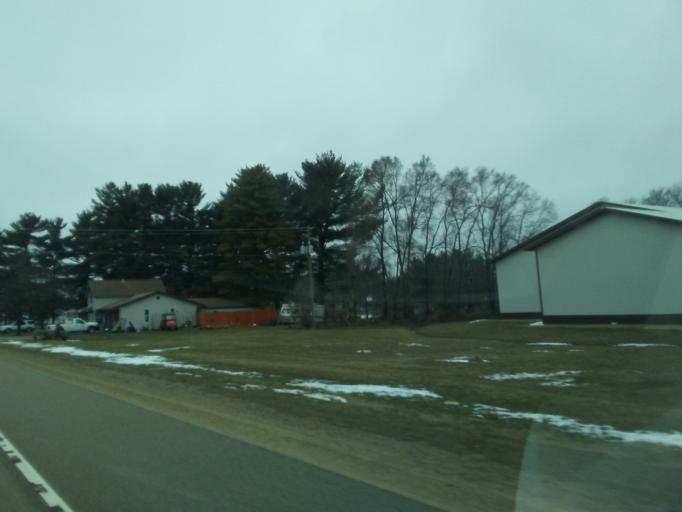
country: US
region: Wisconsin
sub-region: Dane County
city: Mazomanie
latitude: 43.1617
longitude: -89.9097
